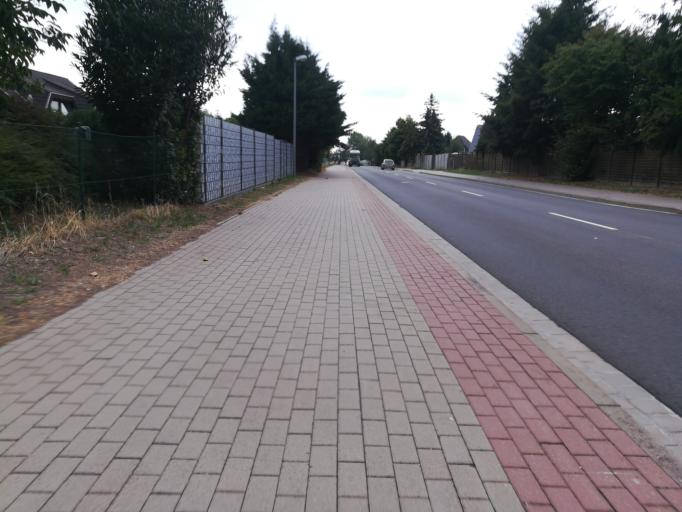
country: DE
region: Saxony-Anhalt
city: Irxleben
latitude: 52.1637
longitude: 11.4883
